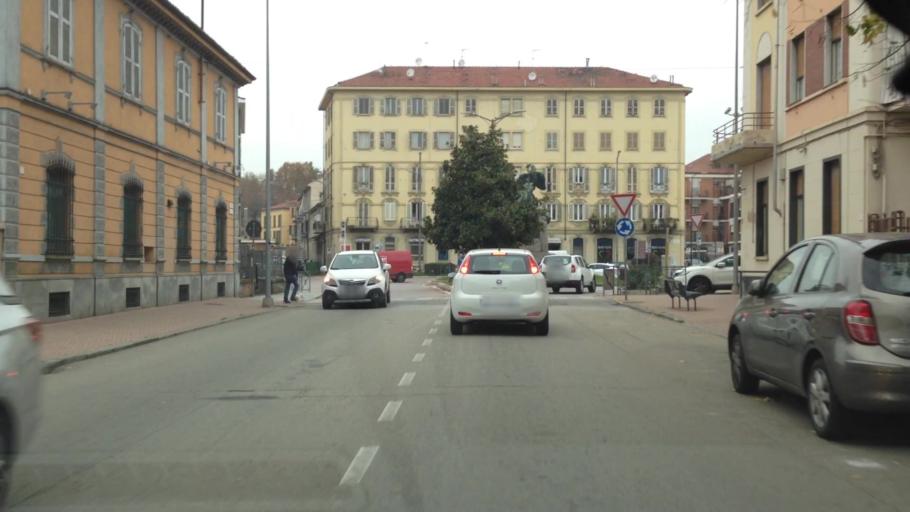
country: IT
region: Piedmont
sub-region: Provincia di Asti
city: Asti
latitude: 44.9024
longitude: 8.2141
